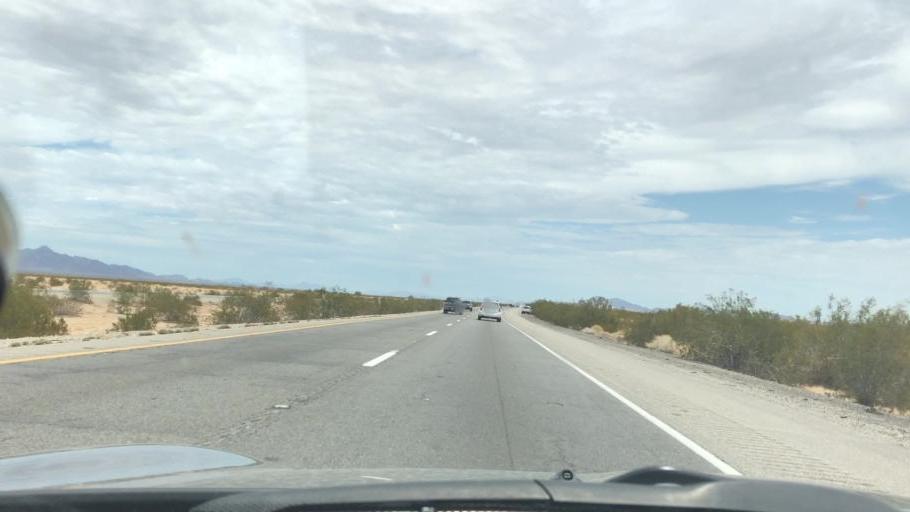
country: US
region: California
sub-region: Riverside County
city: Mesa Verde
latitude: 33.6203
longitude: -115.0355
